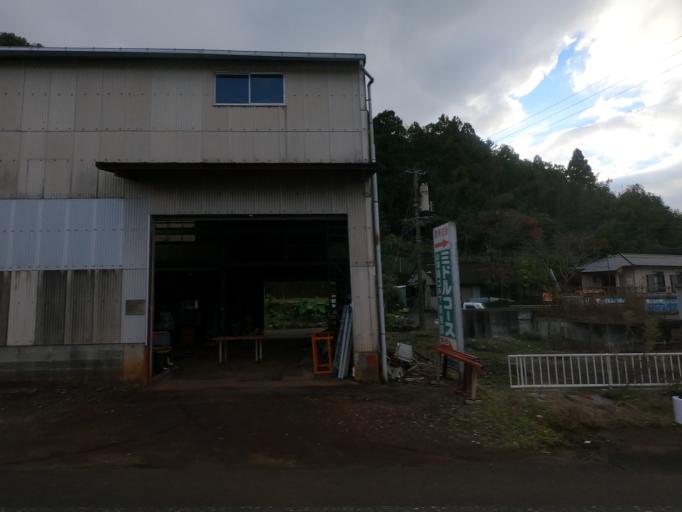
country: JP
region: Kumamoto
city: Minamata
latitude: 32.2674
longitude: 130.5057
